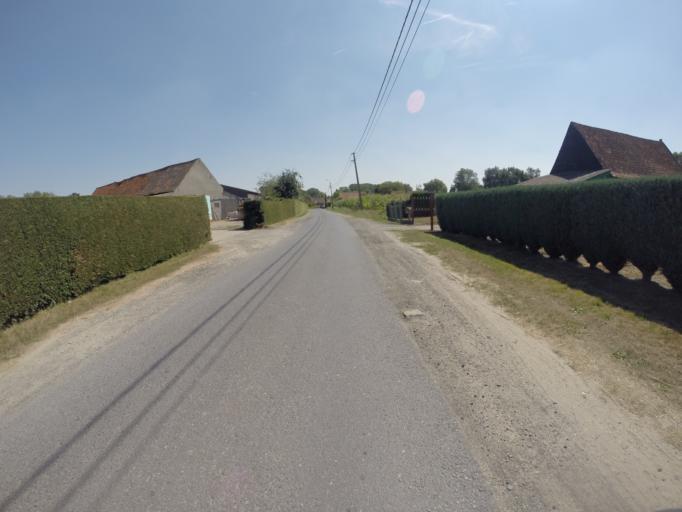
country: BE
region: Flanders
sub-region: Provincie Oost-Vlaanderen
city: Knesselare
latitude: 51.1348
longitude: 3.4419
